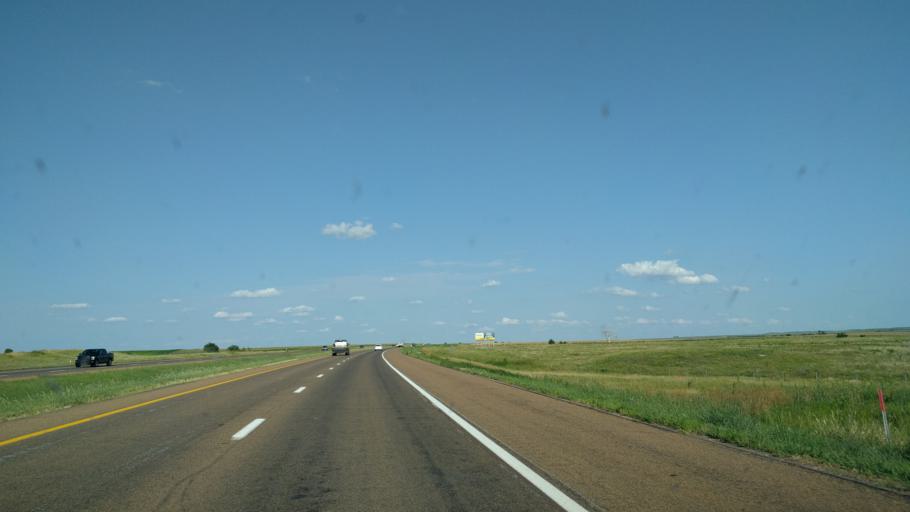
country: US
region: Kansas
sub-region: Ellis County
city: Ellis
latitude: 38.9496
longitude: -99.5264
